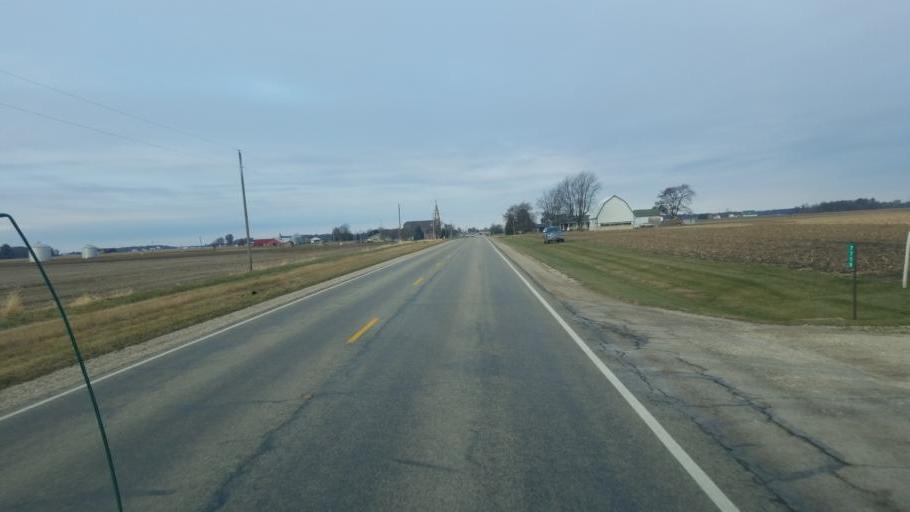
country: US
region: Indiana
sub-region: Adams County
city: Geneva
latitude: 40.5425
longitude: -84.8339
